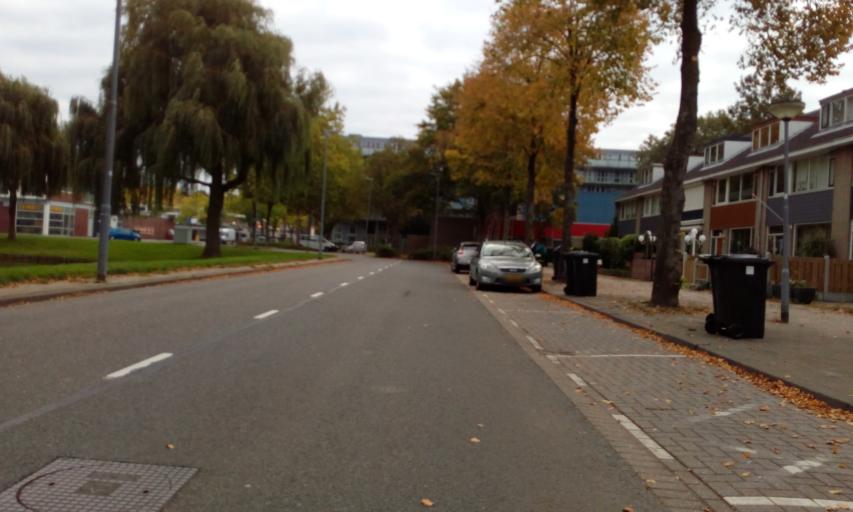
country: NL
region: South Holland
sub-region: Gemeente Spijkenisse
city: Spijkenisse
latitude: 51.8504
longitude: 4.3663
